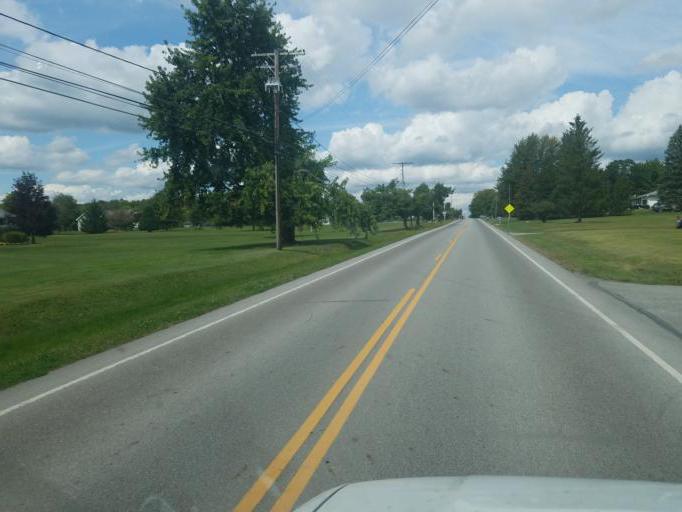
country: US
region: Ohio
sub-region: Geauga County
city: Middlefield
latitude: 41.4163
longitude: -81.0367
